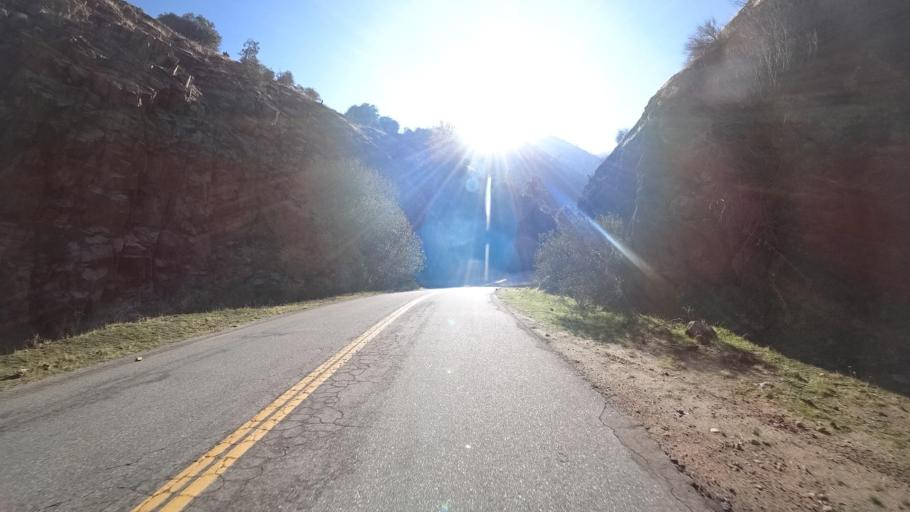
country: US
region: California
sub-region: Kern County
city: Golden Hills
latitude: 35.3152
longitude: -118.5307
